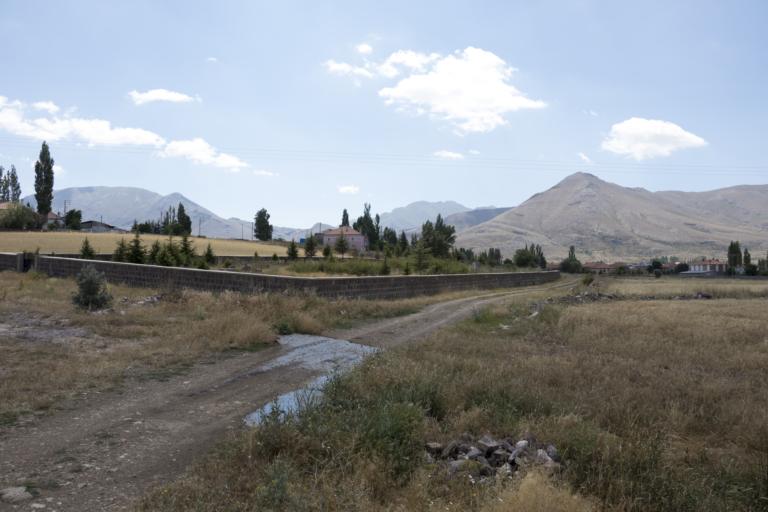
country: TR
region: Kayseri
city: Toklar
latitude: 38.4105
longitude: 36.0768
